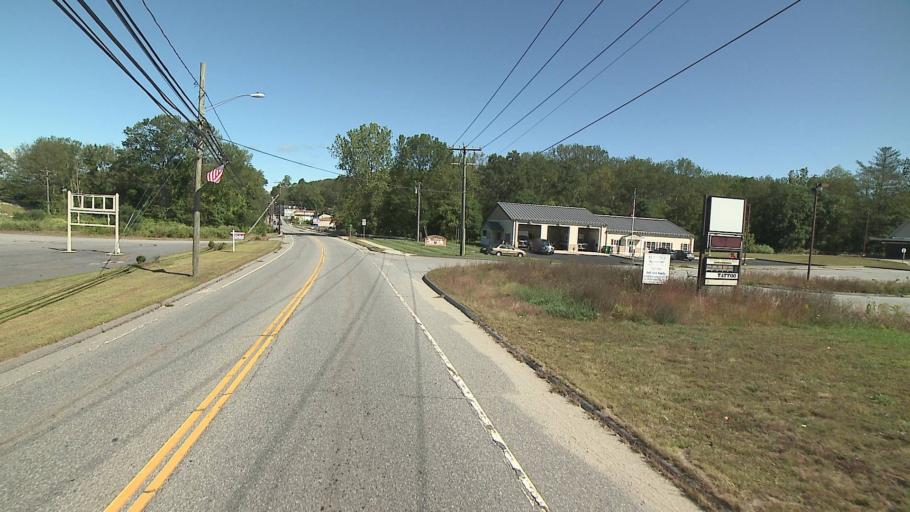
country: US
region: Connecticut
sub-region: Windham County
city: Moosup
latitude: 41.7165
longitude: -71.9031
